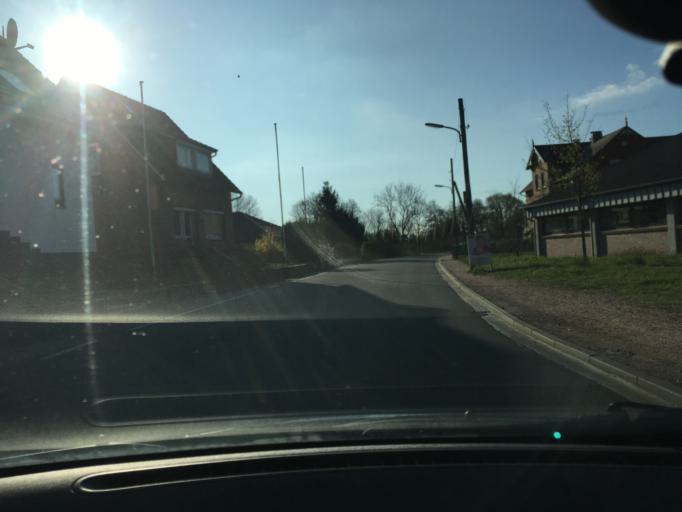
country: DE
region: Hamburg
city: Bergedorf
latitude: 53.4449
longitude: 10.2305
